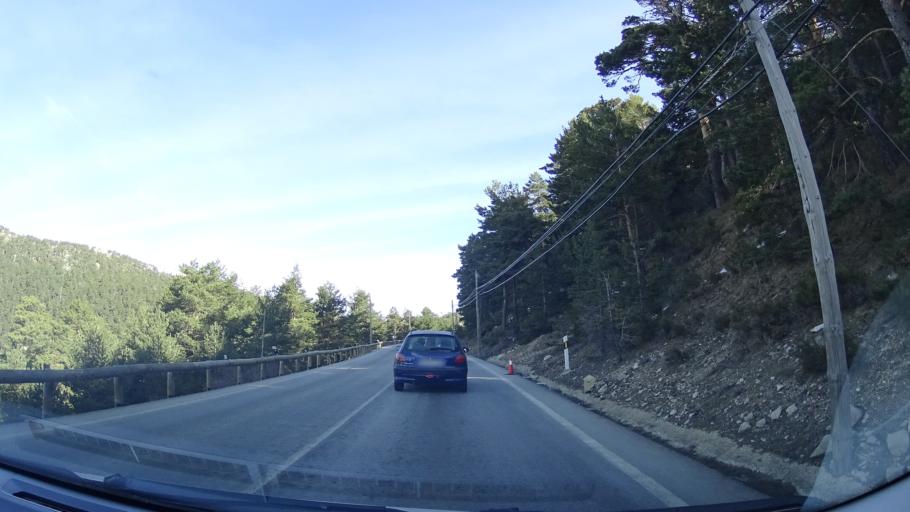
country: ES
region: Madrid
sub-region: Provincia de Madrid
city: Navacerrada
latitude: 40.7773
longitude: -4.0049
